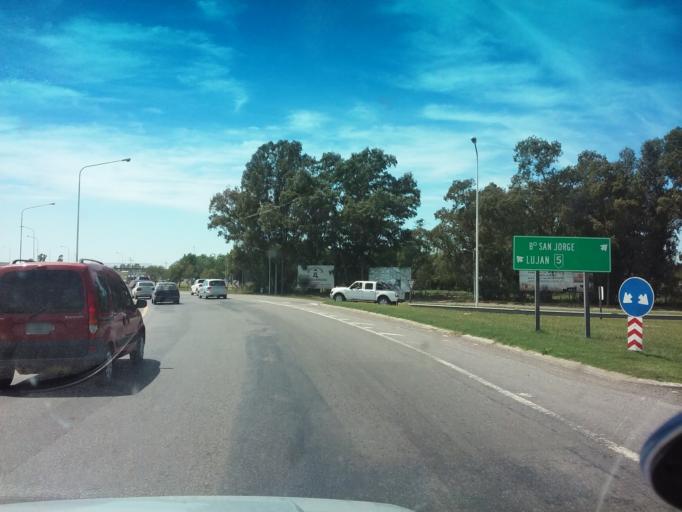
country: AR
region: Buenos Aires
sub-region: Partido de Mercedes
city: Mercedes
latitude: -34.6673
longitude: -59.4080
